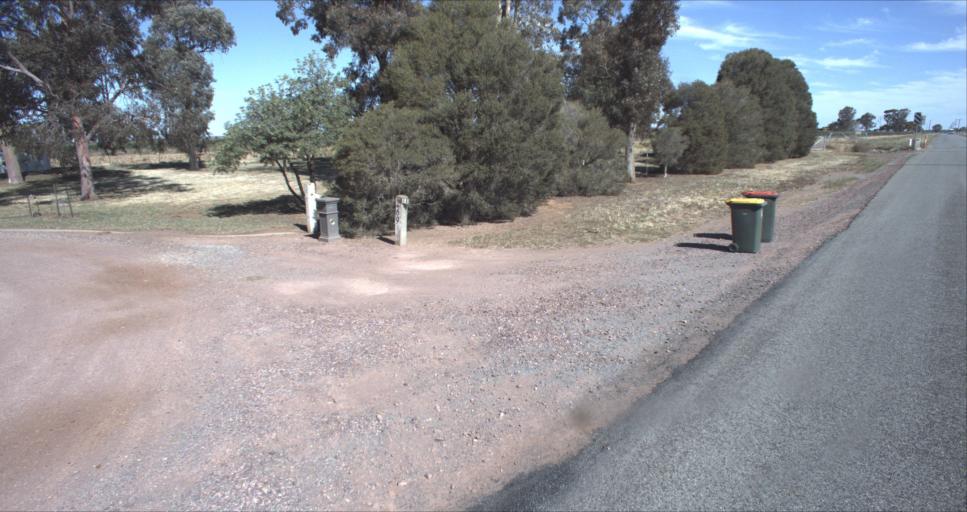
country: AU
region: New South Wales
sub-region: Leeton
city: Leeton
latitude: -34.5691
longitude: 146.3820
